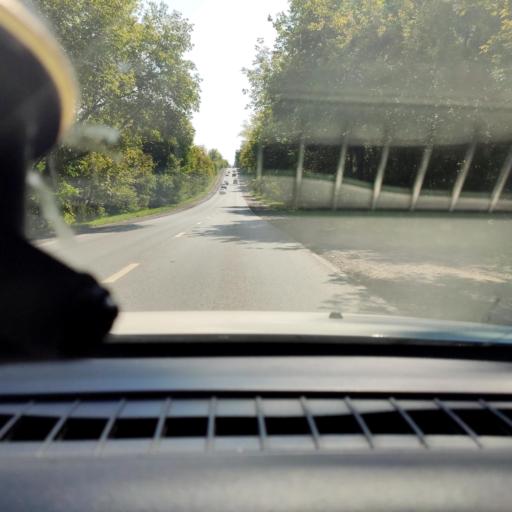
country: RU
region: Samara
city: Novosemeykino
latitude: 53.3213
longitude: 50.2656
